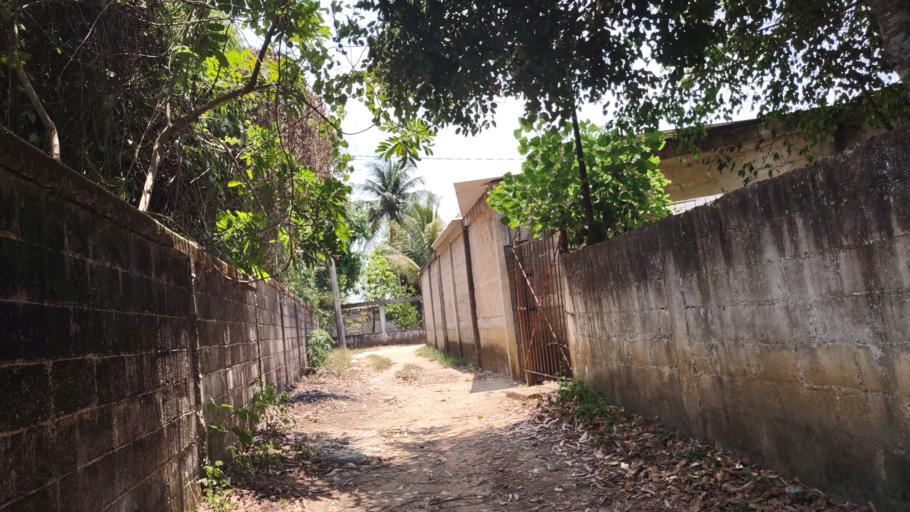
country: MX
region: Veracruz
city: Las Choapas
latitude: 17.9249
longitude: -94.0957
